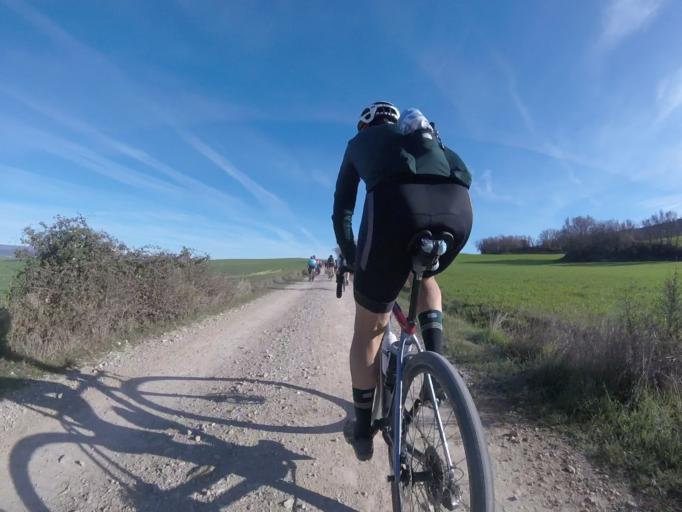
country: ES
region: Navarre
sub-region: Provincia de Navarra
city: Villatuerta
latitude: 42.6557
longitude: -1.9704
